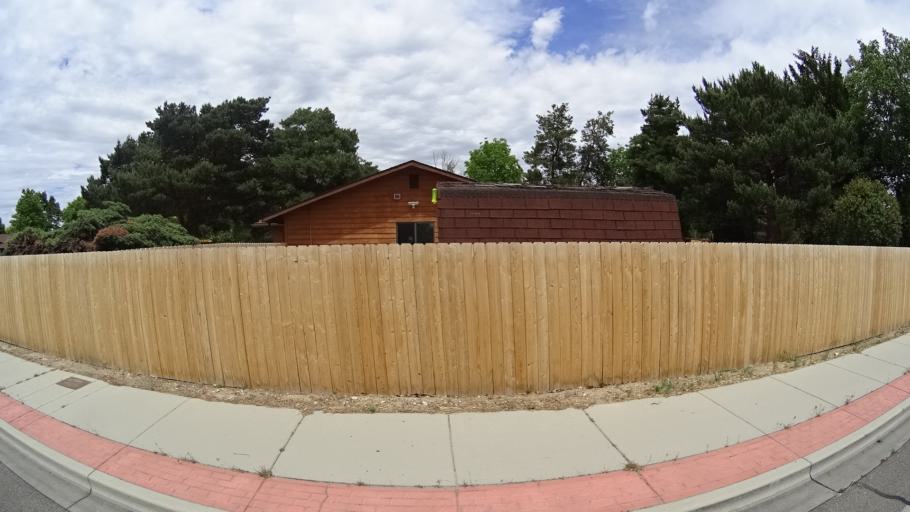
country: US
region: Idaho
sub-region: Ada County
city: Meridian
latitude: 43.5903
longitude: -116.3184
